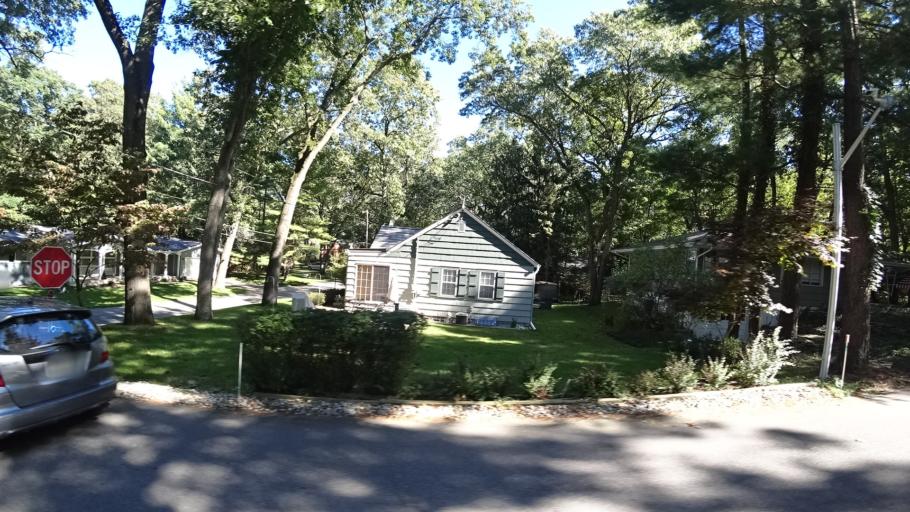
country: US
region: Indiana
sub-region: LaPorte County
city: Long Beach
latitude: 41.7538
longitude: -86.8316
